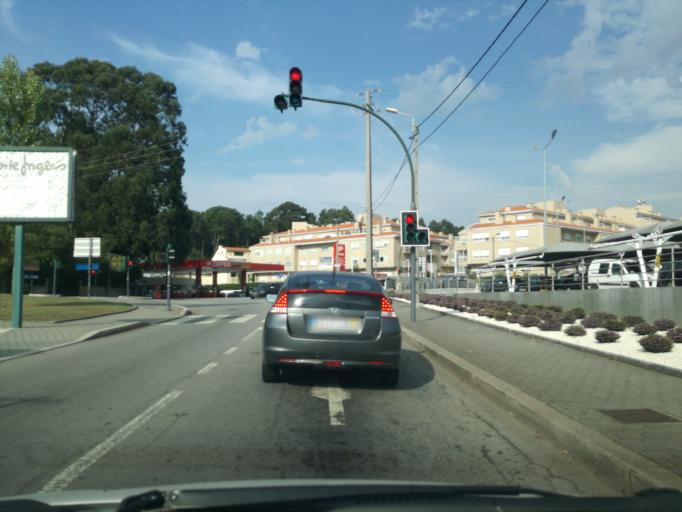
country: PT
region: Porto
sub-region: Vila Nova de Gaia
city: Azenha
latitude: 41.0697
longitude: -8.6259
